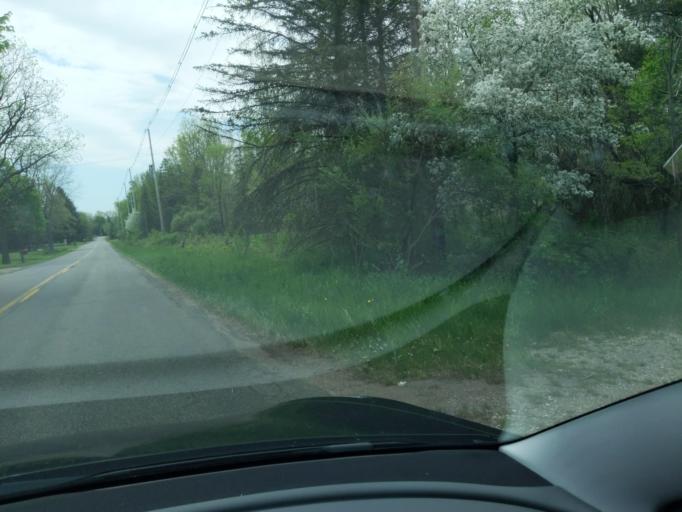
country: US
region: Michigan
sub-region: Ingham County
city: Holt
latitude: 42.6456
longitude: -84.5530
